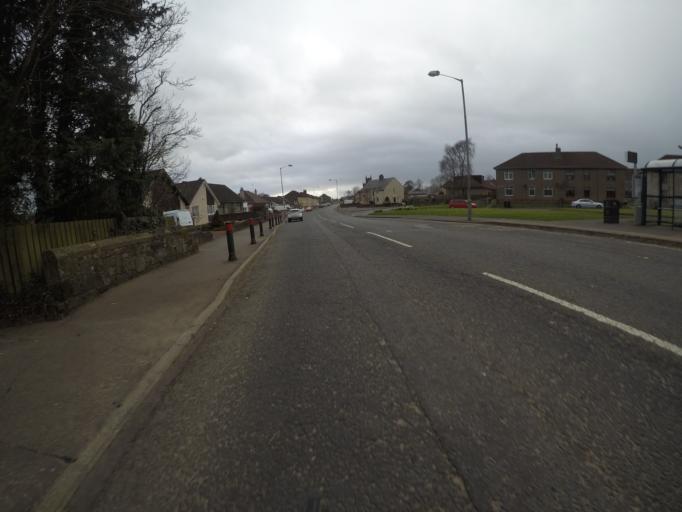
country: GB
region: Scotland
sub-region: East Ayrshire
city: Crosshouse
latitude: 55.6125
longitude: -4.5470
